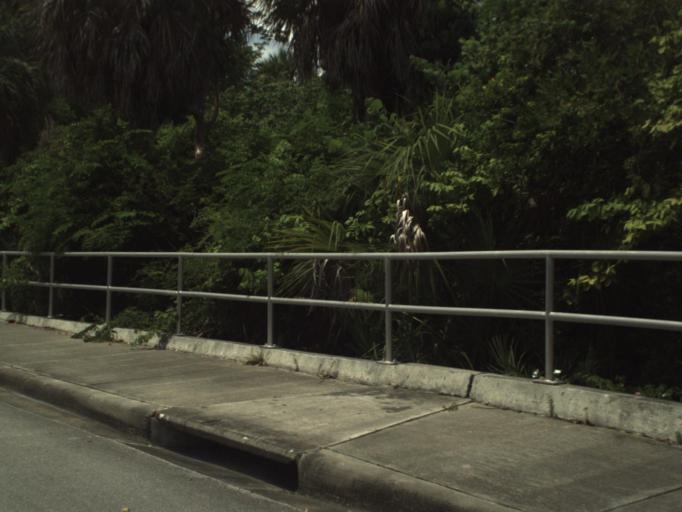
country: US
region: Florida
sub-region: Palm Beach County
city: Lake Park
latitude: 26.8236
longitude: -80.0442
